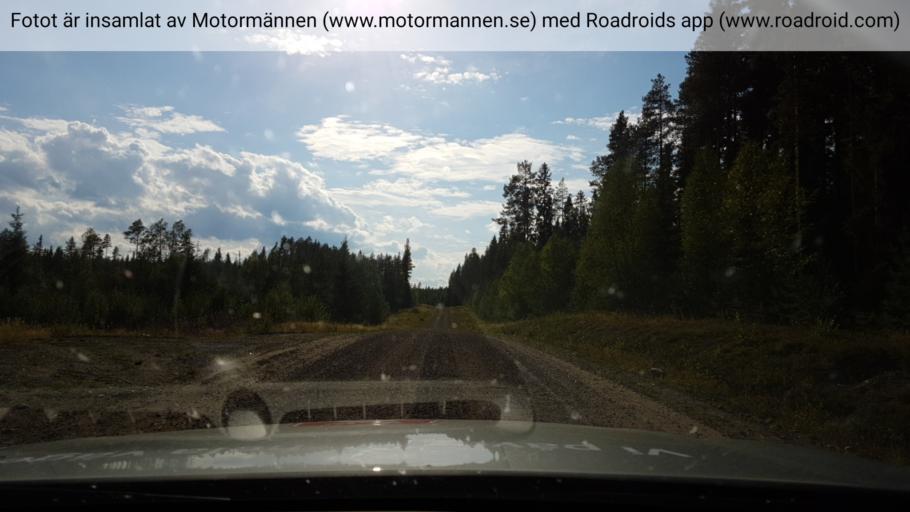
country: SE
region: Jaemtland
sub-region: Stroemsunds Kommun
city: Stroemsund
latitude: 63.7273
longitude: 16.1090
